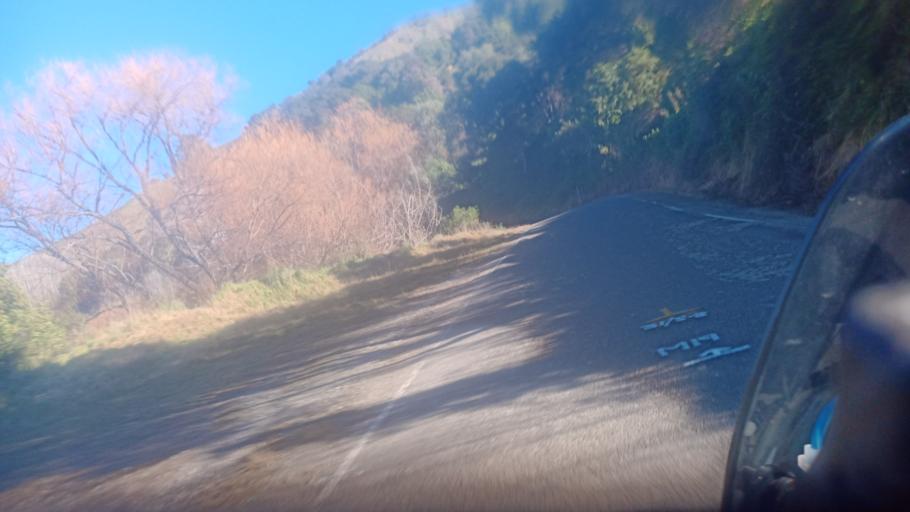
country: NZ
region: Gisborne
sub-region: Gisborne District
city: Gisborne
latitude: -38.5604
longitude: 177.6203
